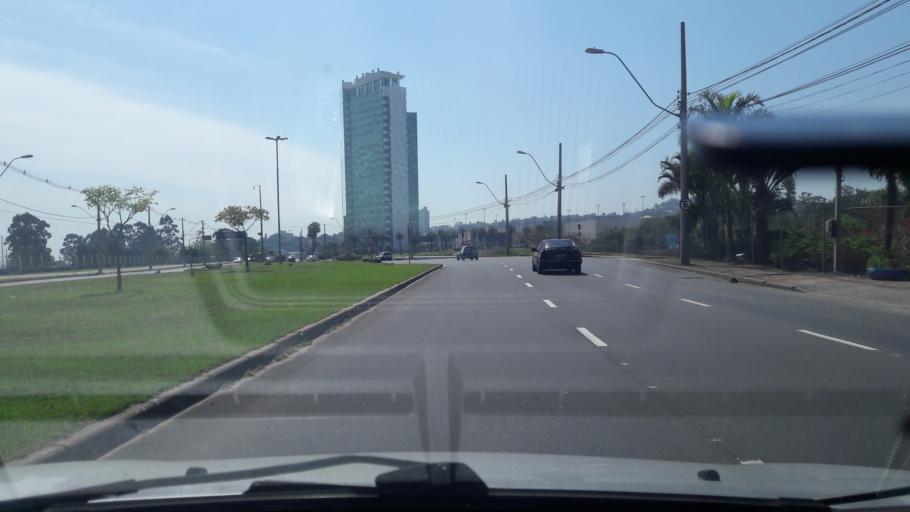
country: BR
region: Rio Grande do Sul
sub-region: Porto Alegre
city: Porto Alegre
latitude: -30.0896
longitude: -51.2485
